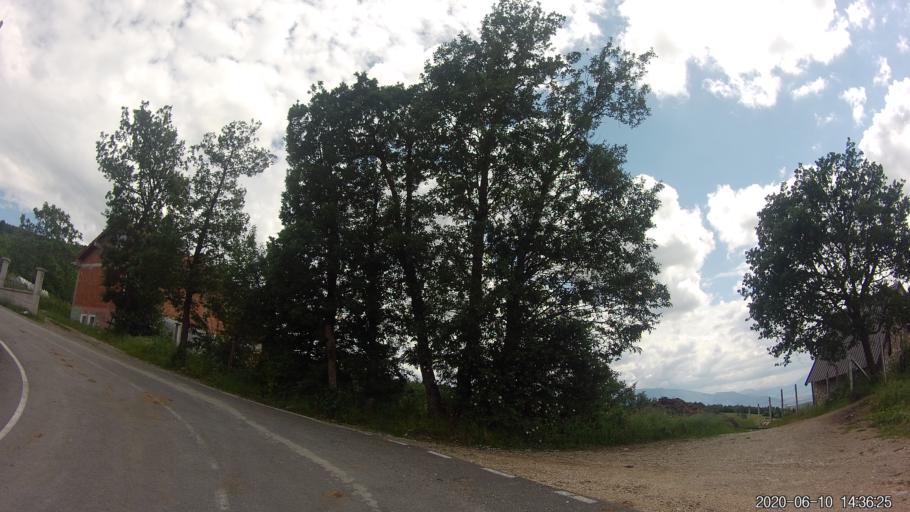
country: XK
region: Prizren
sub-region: Komuna e Therandes
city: Budakovo
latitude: 42.4106
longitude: 20.9376
